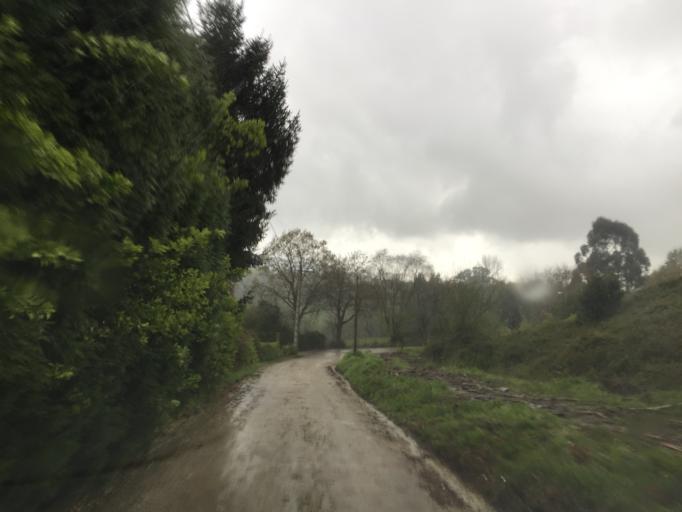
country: ES
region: Asturias
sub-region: Province of Asturias
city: Arriba
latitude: 43.5275
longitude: -5.5858
